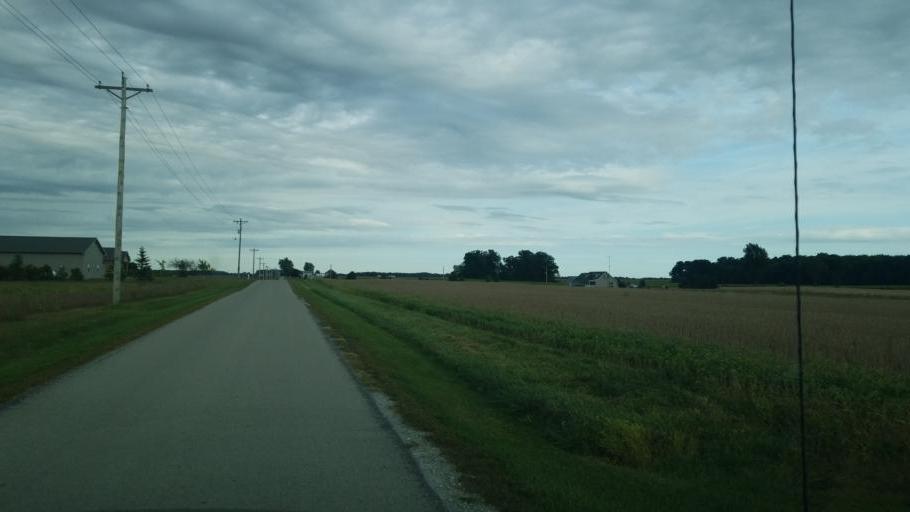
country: US
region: Ohio
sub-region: Wyandot County
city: Carey
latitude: 40.9152
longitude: -83.3022
